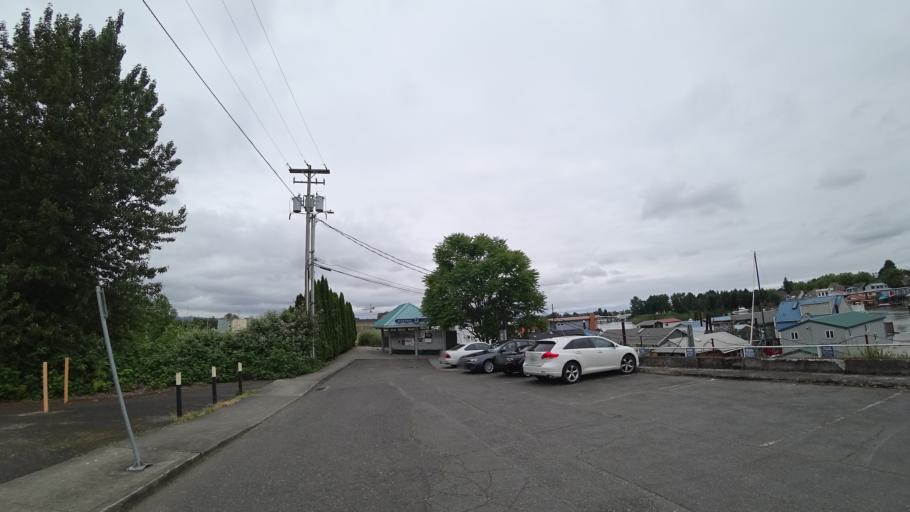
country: US
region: Washington
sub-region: Clark County
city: Vancouver
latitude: 45.6034
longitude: -122.6708
